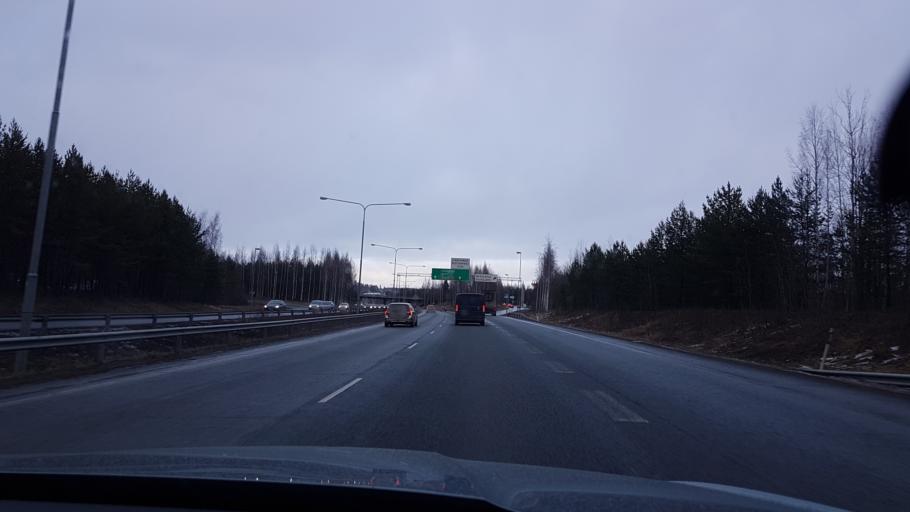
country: FI
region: Pirkanmaa
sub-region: Tampere
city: Tampere
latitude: 61.4739
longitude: 23.8675
